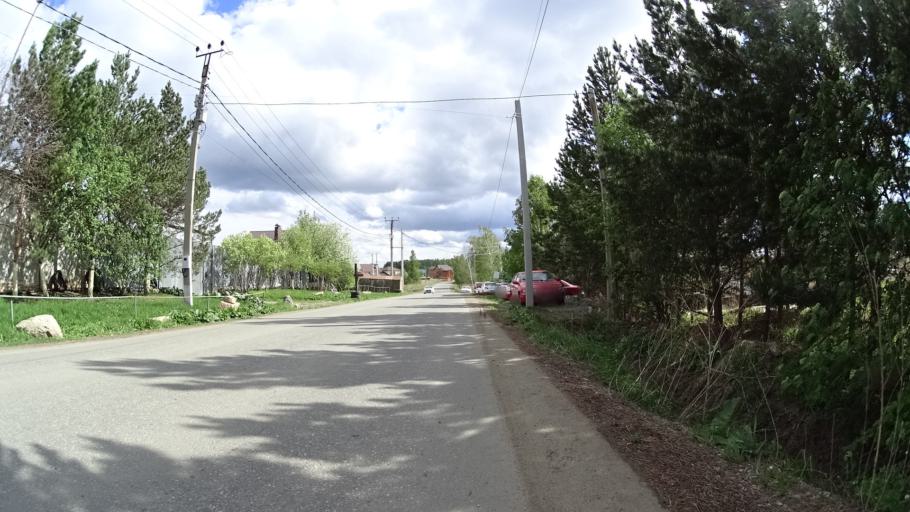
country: RU
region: Chelyabinsk
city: Sargazy
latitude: 55.1568
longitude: 61.2414
